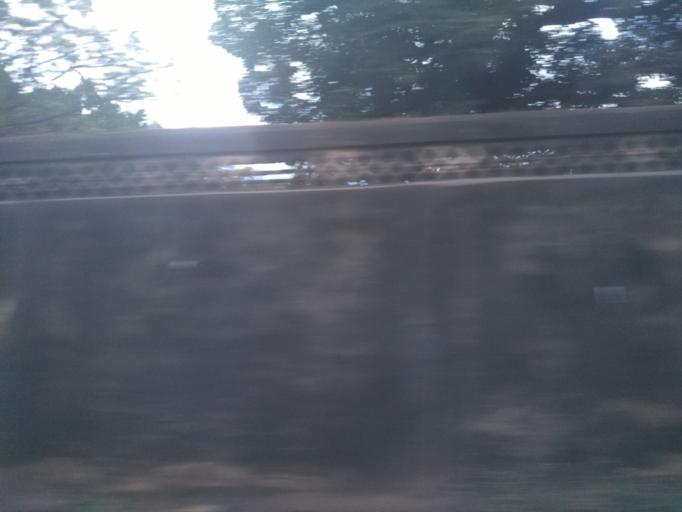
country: TZ
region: Dar es Salaam
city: Magomeni
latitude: -6.7860
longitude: 39.2705
